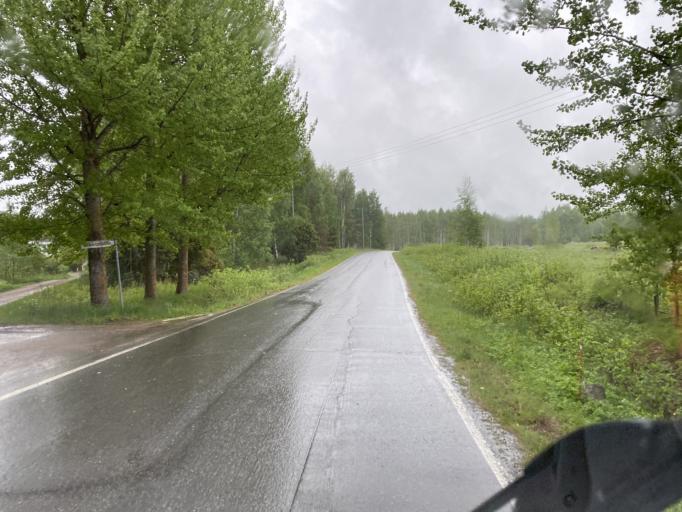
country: FI
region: Haeme
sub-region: Forssa
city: Humppila
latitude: 61.0666
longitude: 23.3214
